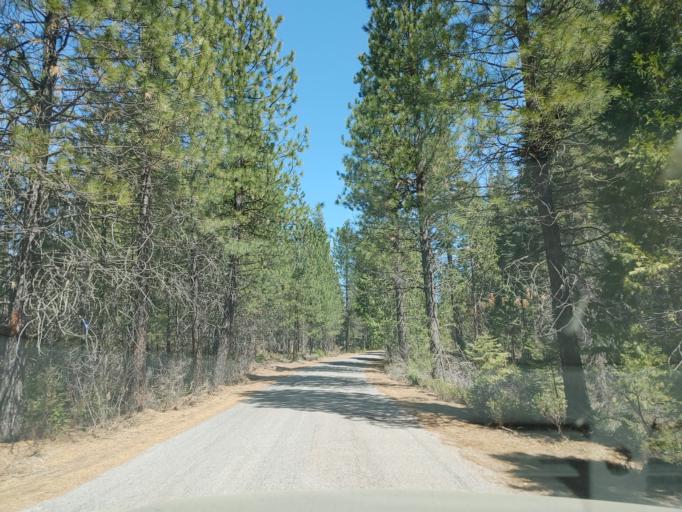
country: US
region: California
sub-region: Siskiyou County
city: McCloud
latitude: 41.2474
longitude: -121.9614
